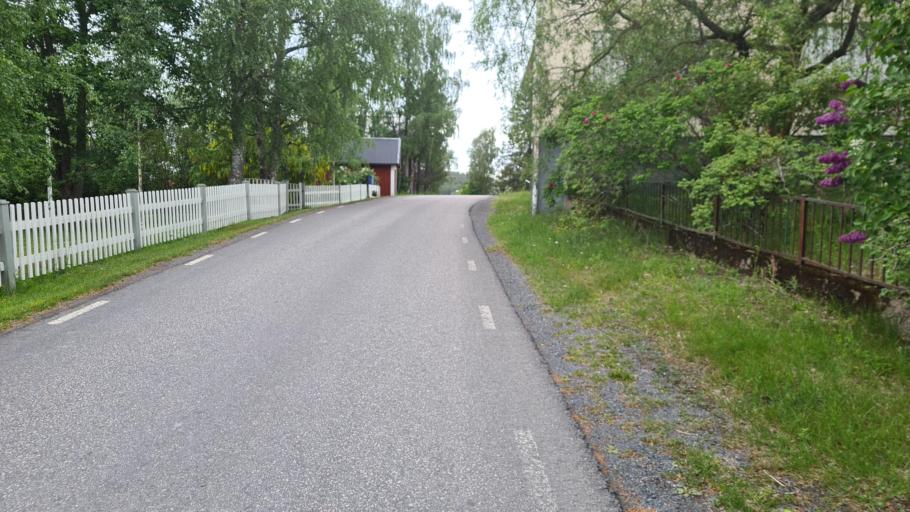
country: SE
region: Vaesternorrland
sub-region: Kramfors Kommun
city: Nordingra
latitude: 62.9829
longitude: 18.4323
